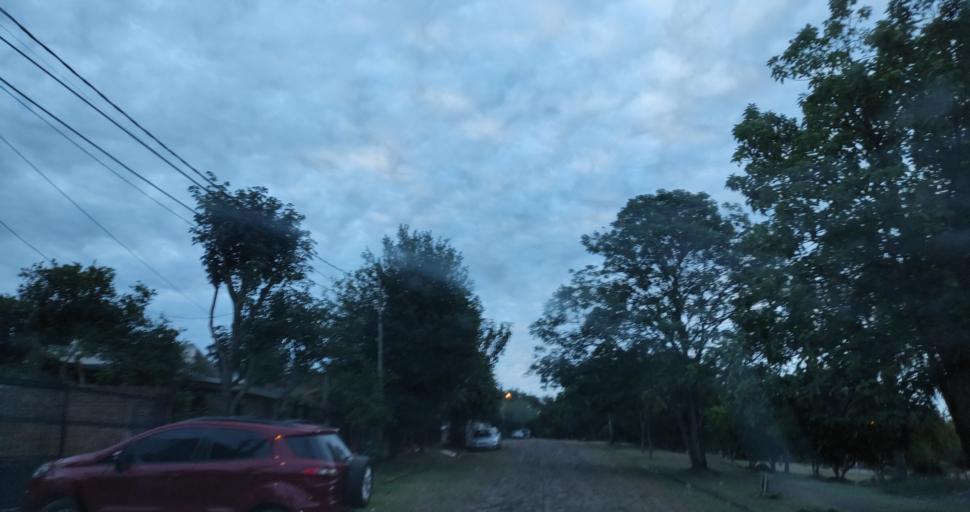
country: AR
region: Misiones
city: Garupa
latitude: -27.4725
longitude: -55.8464
